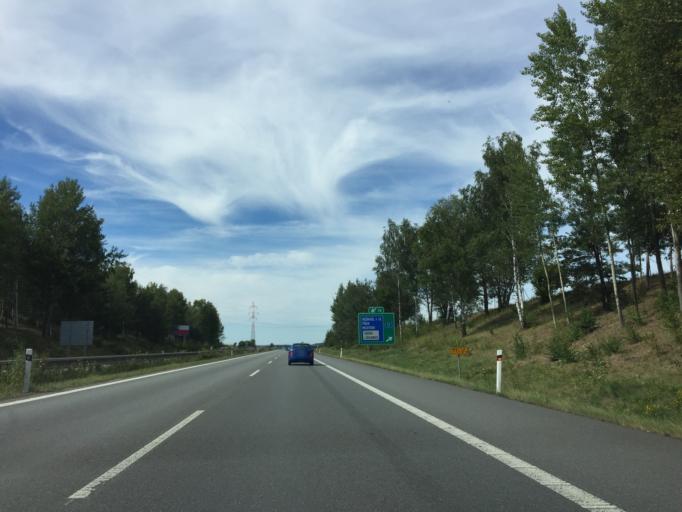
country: CZ
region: Jihocesky
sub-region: Okres Tabor
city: Sezimovo Usti
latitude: 49.4236
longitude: 14.7025
